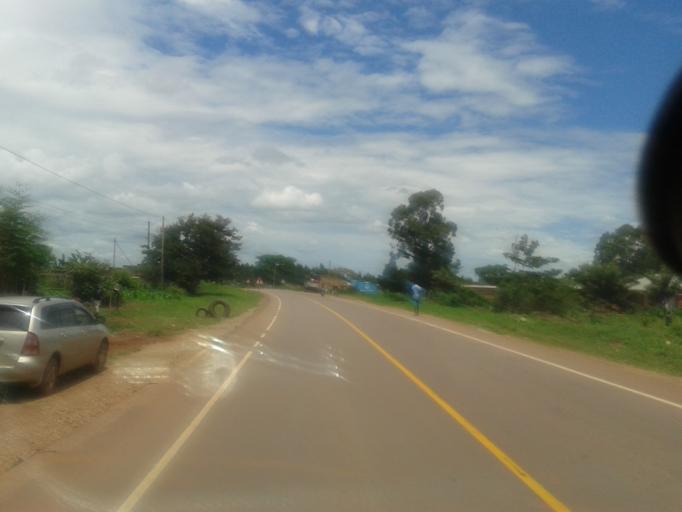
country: UG
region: Western Region
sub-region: Kiryandongo District
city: Kiryandongo
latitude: 1.8024
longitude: 32.0097
